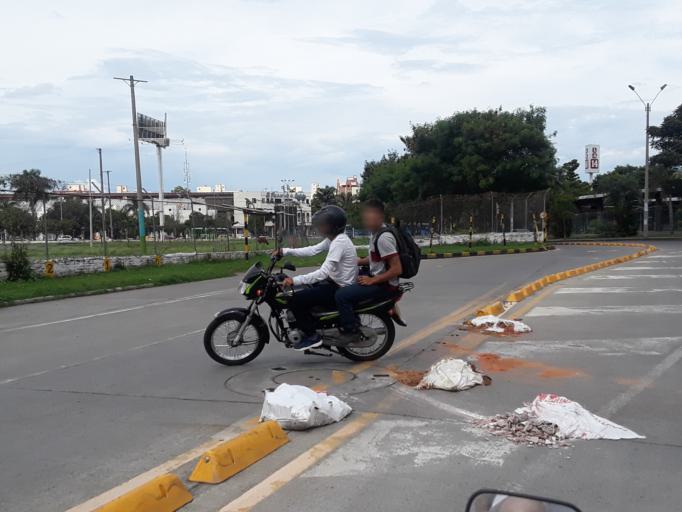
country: CO
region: Valle del Cauca
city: Cali
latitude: 3.4158
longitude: -76.5498
